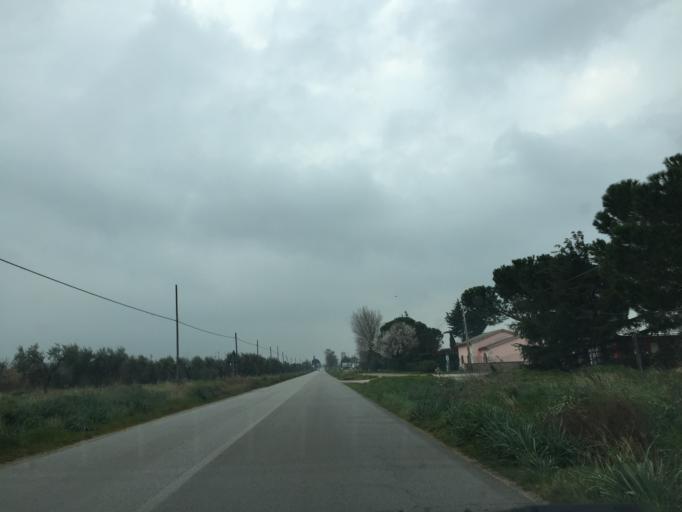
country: IT
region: Apulia
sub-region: Provincia di Foggia
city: Foggia
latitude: 41.4310
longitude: 15.4739
